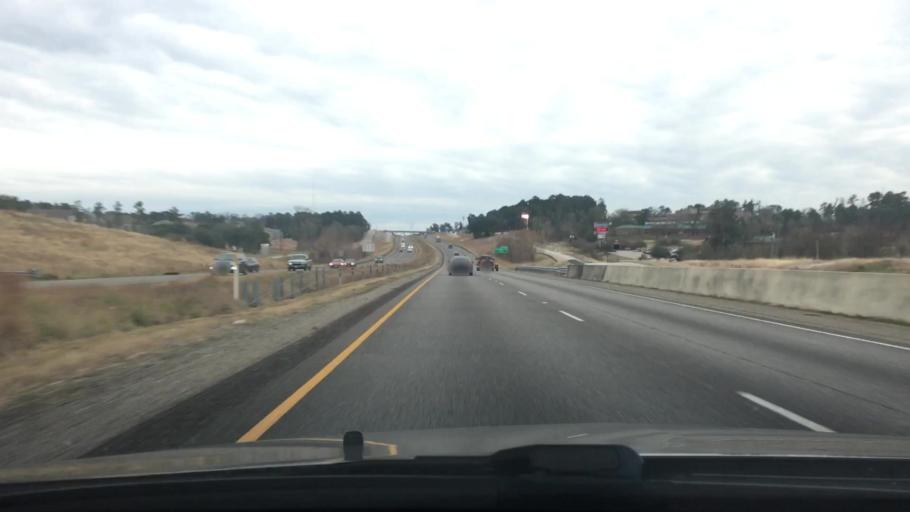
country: US
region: Texas
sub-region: Walker County
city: Huntsville
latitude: 30.7051
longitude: -95.5611
